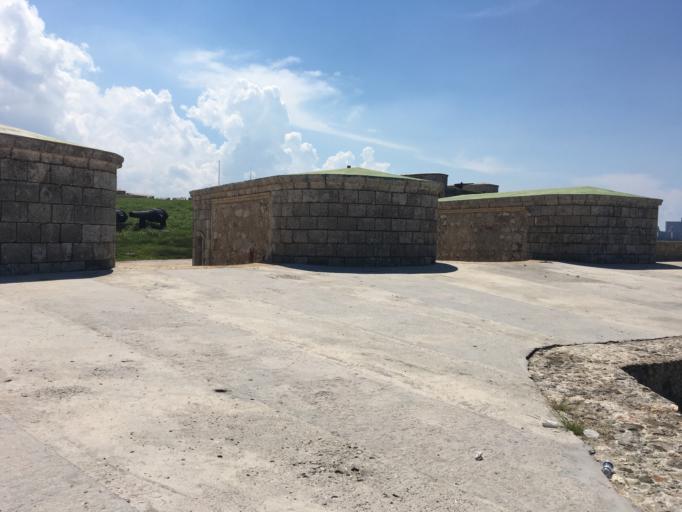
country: CU
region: La Habana
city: Centro Habana
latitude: 23.1520
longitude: -82.3555
